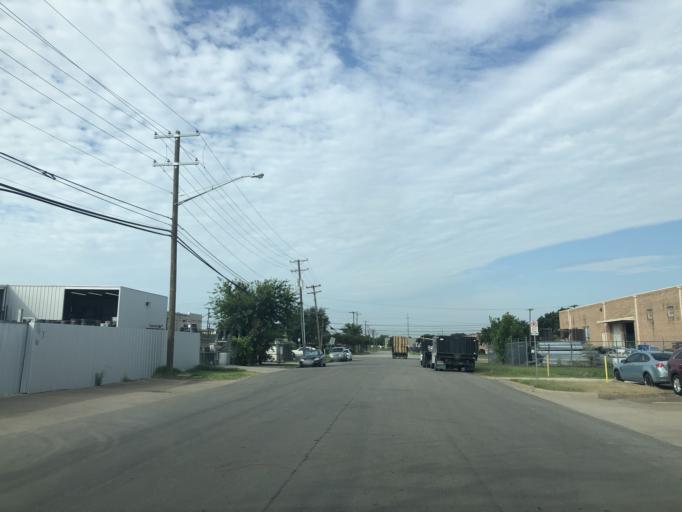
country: US
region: Texas
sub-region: Dallas County
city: Irving
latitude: 32.8173
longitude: -96.8828
